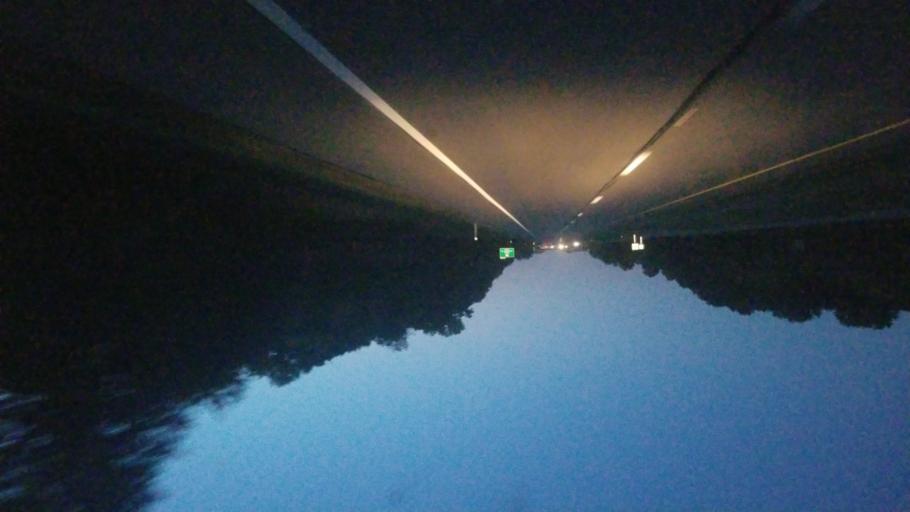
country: US
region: Ohio
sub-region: Ashtabula County
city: Roaming Shores
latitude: 41.5476
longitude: -80.7136
